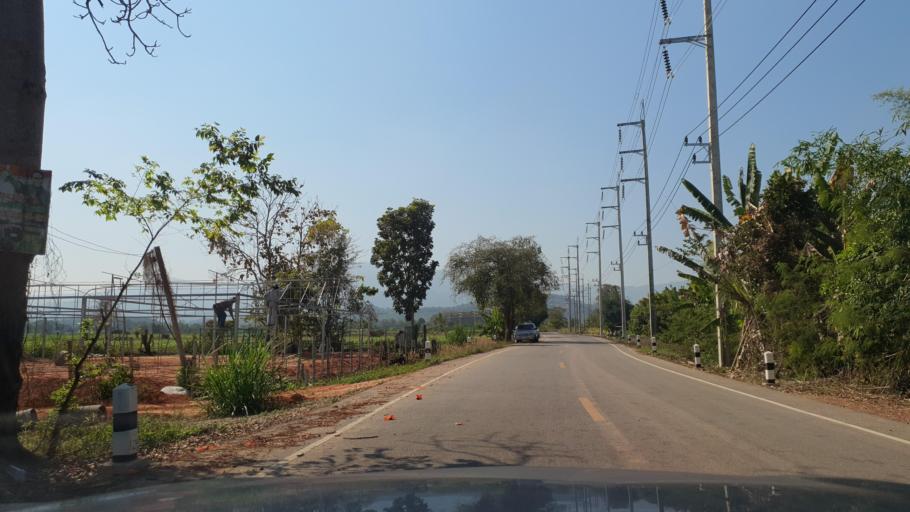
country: TH
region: Chiang Rai
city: Mae Lao
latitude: 19.8035
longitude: 99.6905
